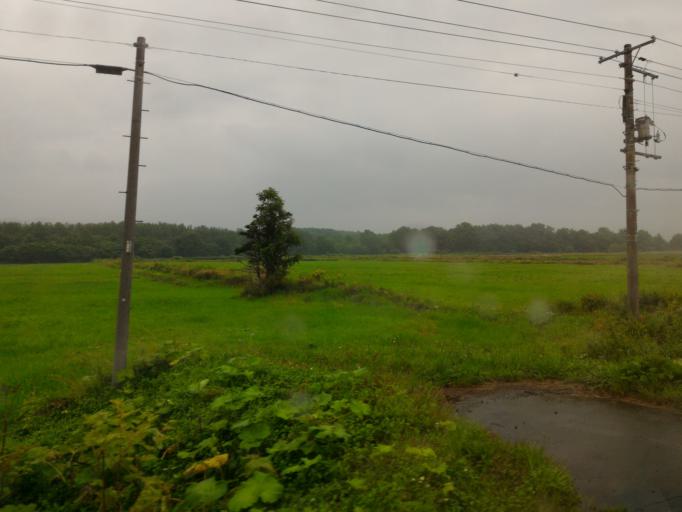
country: JP
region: Hokkaido
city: Nayoro
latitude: 44.5191
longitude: 142.3284
